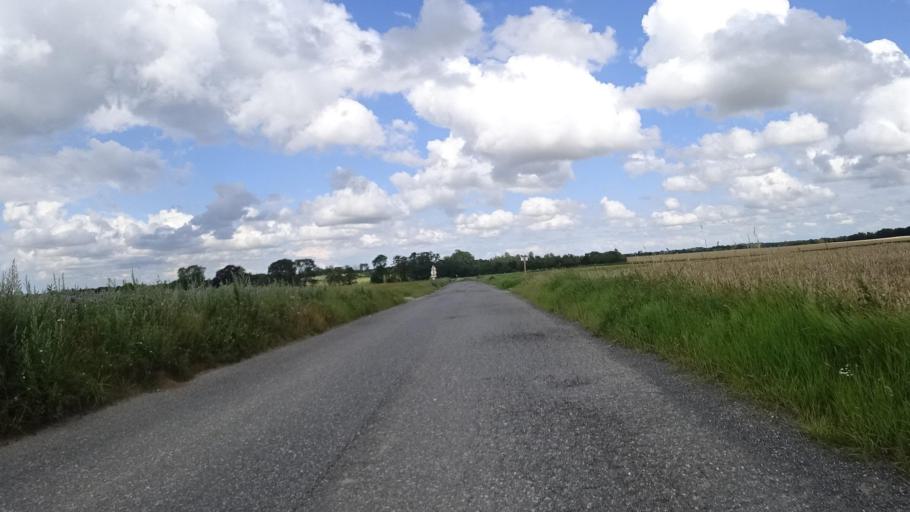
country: BE
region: Wallonia
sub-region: Province du Brabant Wallon
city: Villers-la-Ville
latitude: 50.5557
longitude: 4.5203
